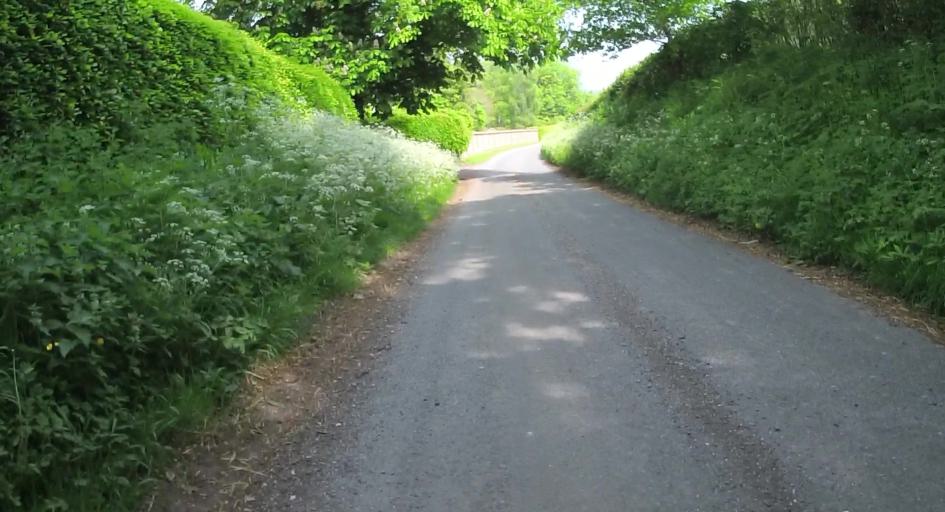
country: GB
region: England
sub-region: Hampshire
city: Kingsclere
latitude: 51.2828
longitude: -1.2326
